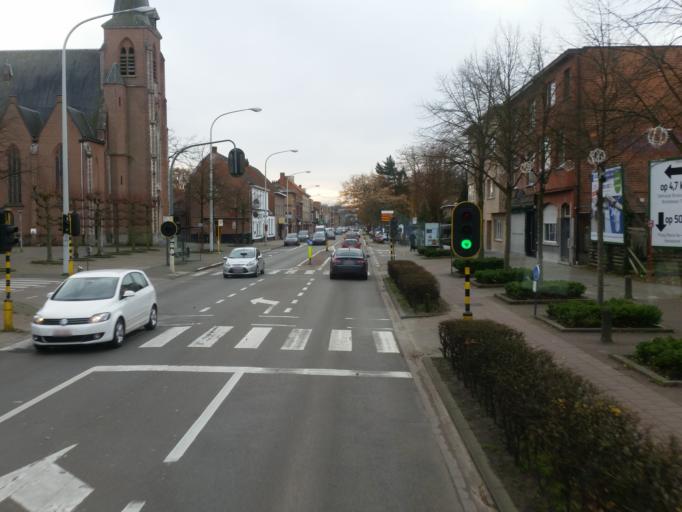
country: BE
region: Flanders
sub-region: Provincie Antwerpen
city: Brasschaat
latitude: 51.3239
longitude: 4.5204
